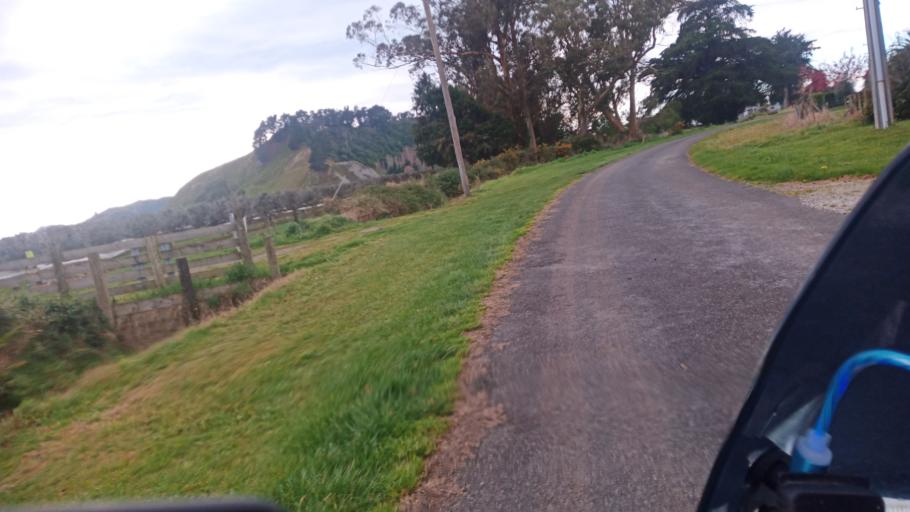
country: NZ
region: Gisborne
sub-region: Gisborne District
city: Gisborne
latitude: -38.3698
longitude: 178.2871
